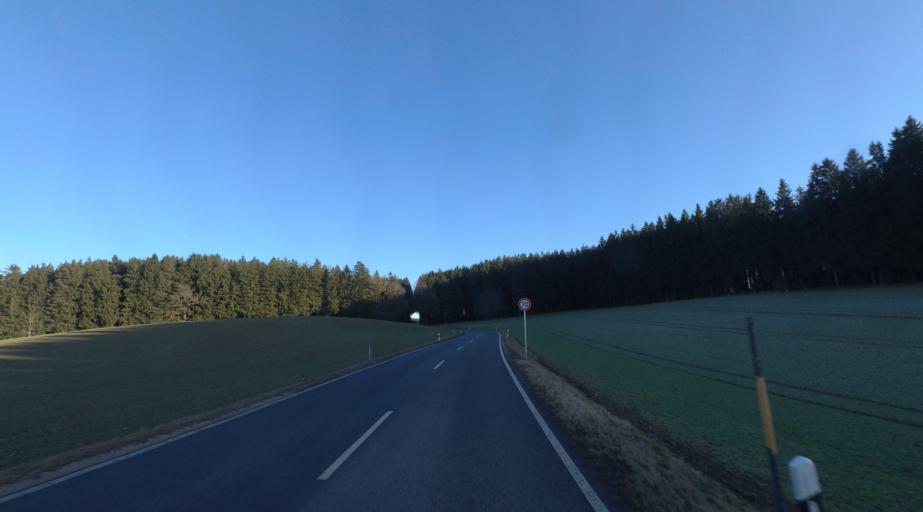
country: DE
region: Bavaria
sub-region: Upper Bavaria
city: Trostberg an der Alz
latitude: 48.0181
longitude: 12.5953
